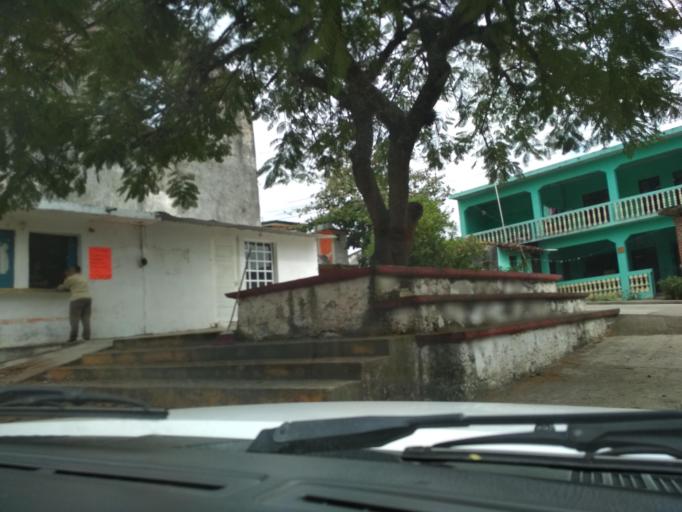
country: MX
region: Veracruz
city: Alto Lucero
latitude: 19.5910
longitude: -96.7823
